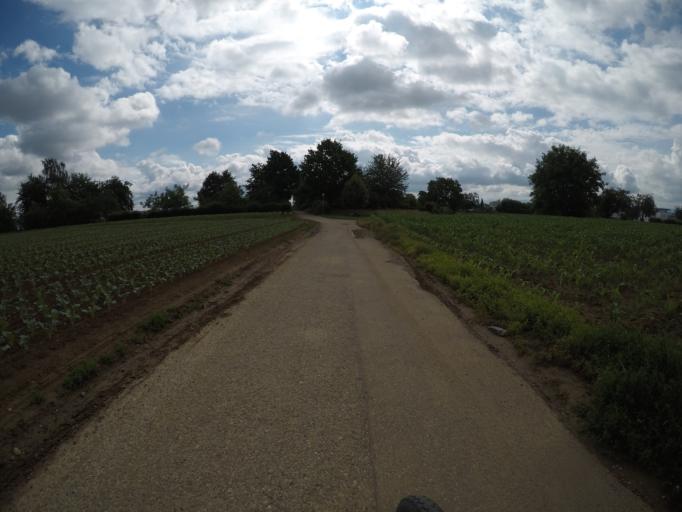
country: DE
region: Baden-Wuerttemberg
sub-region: Regierungsbezirk Stuttgart
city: Esslingen
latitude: 48.7223
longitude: 9.2943
